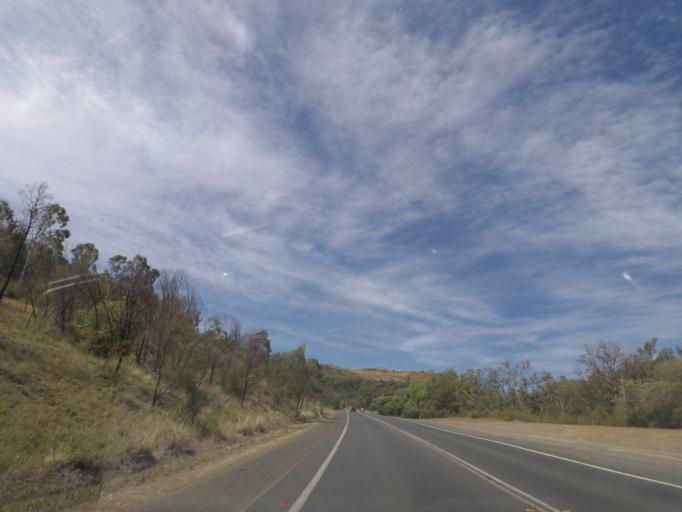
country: AU
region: New South Wales
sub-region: Wollondilly
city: Picton
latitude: -34.1622
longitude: 150.6400
